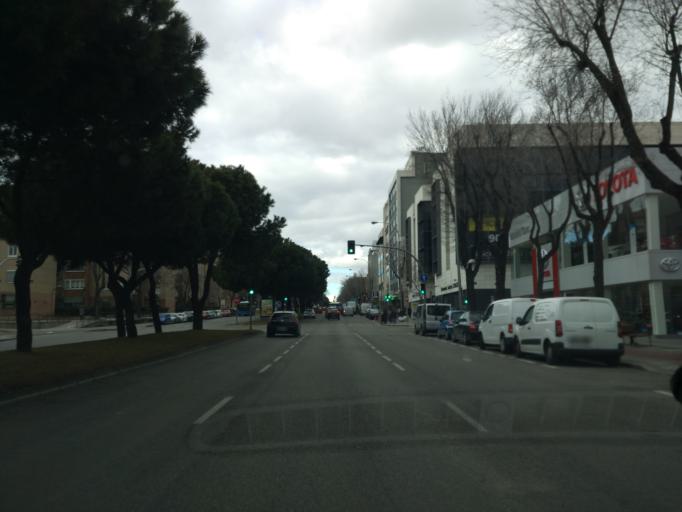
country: ES
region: Madrid
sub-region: Provincia de Madrid
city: San Blas
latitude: 40.4308
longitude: -3.6327
